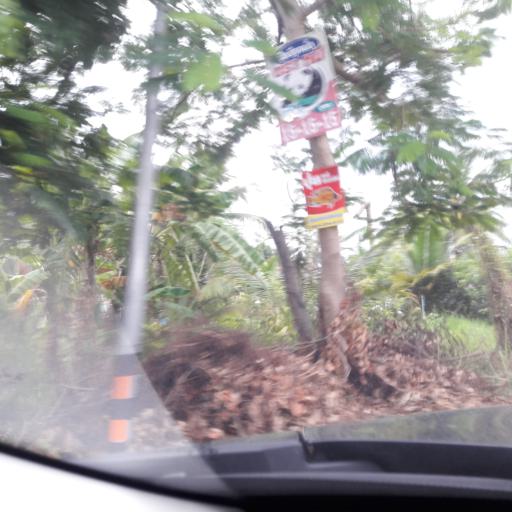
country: TH
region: Ratchaburi
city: Damnoen Saduak
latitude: 13.5827
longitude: 99.9498
